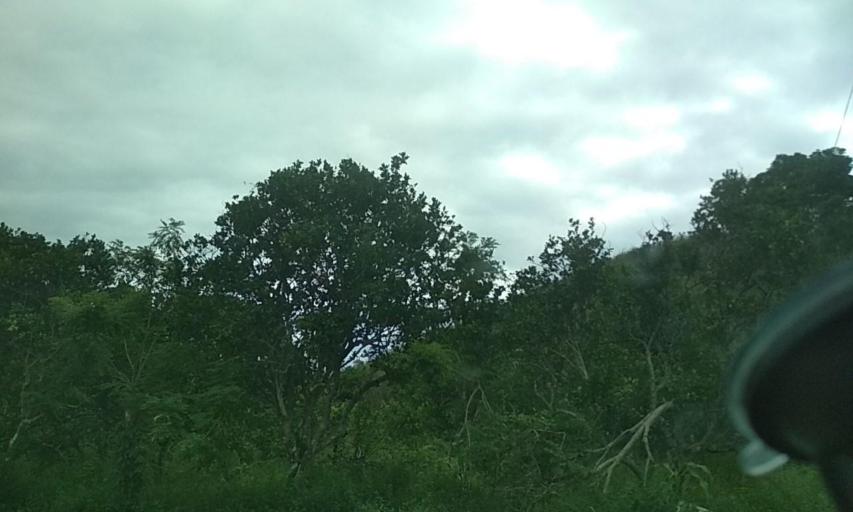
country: MX
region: Veracruz
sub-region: Papantla
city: Polutla
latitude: 20.5813
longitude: -97.2769
